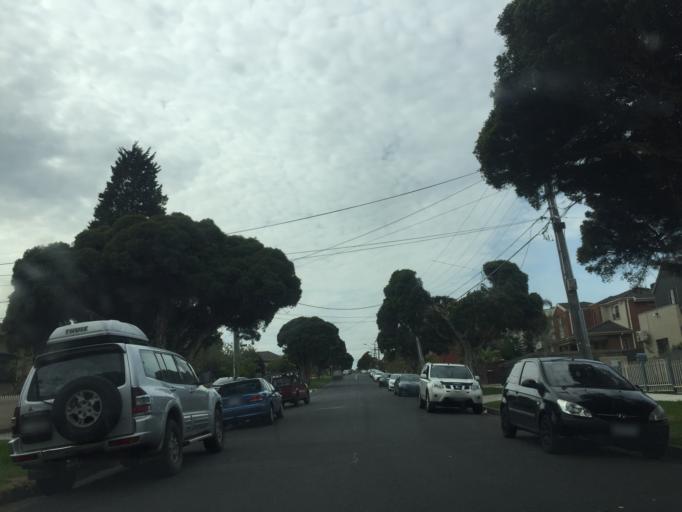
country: AU
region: Victoria
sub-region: Darebin
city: Preston
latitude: -37.7570
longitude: 145.0158
